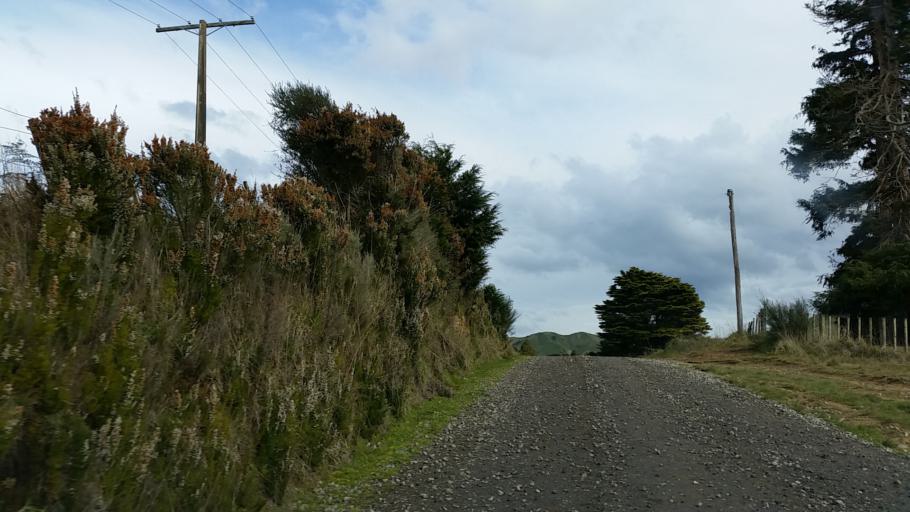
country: NZ
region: Taranaki
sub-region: South Taranaki District
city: Eltham
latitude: -39.4116
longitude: 174.4479
